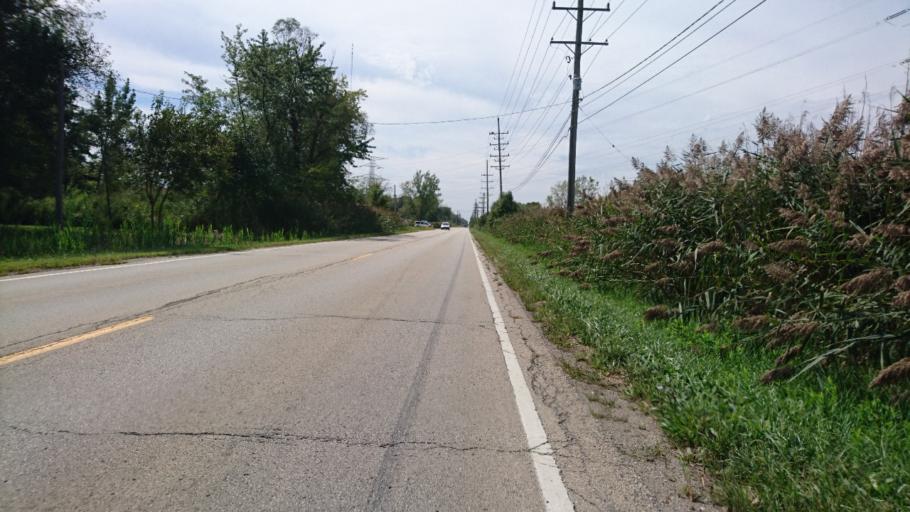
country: US
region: Illinois
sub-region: Will County
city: Wilmington
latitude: 41.2990
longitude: -88.1675
